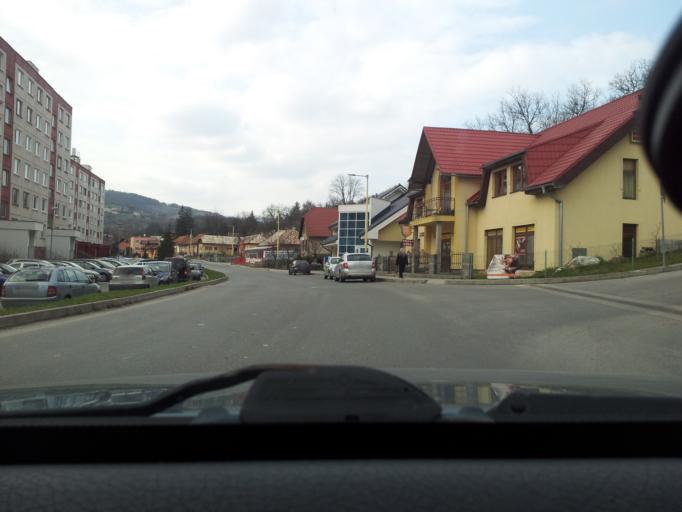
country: SK
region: Banskobystricky
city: Nova Bana
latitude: 48.4244
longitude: 18.6421
